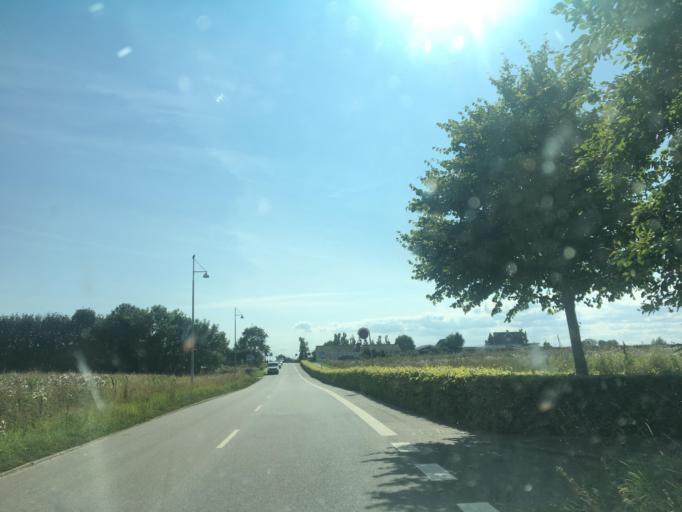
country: DK
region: South Denmark
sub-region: Middelfart Kommune
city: Strib
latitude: 55.4872
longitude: 9.7869
